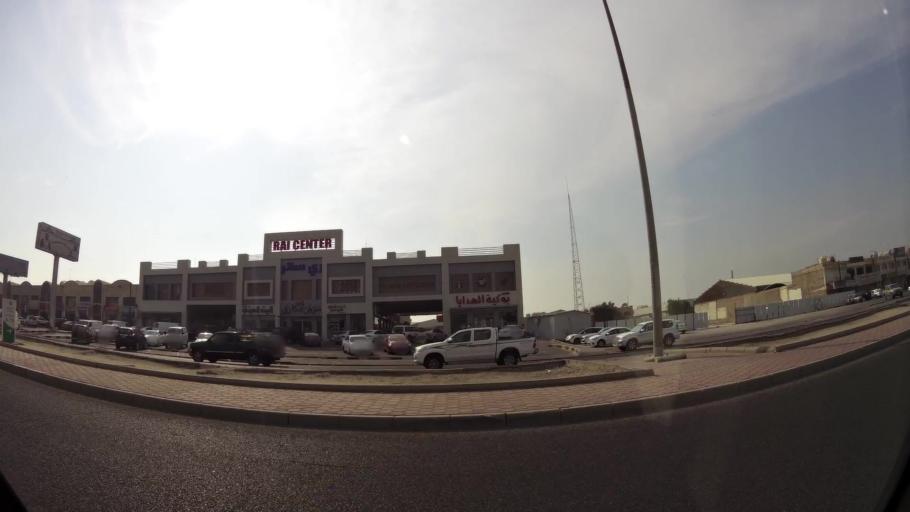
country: KW
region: Al Asimah
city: Ar Rabiyah
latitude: 29.3107
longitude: 47.9480
